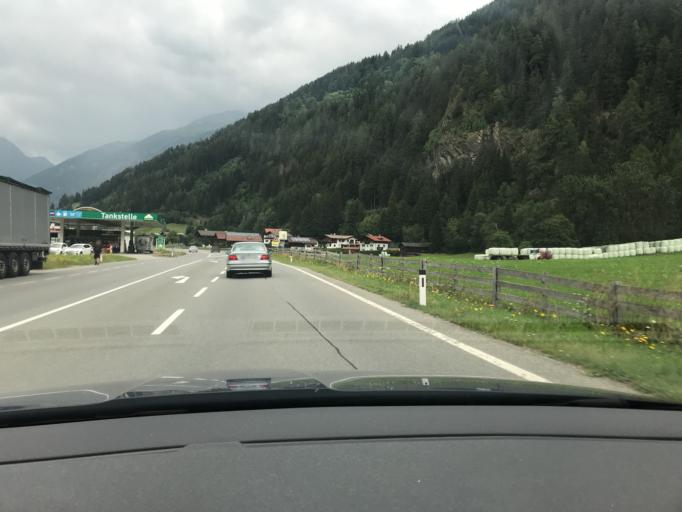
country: AT
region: Tyrol
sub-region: Politischer Bezirk Lienz
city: Matrei in Osttirol
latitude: 46.9804
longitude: 12.5503
